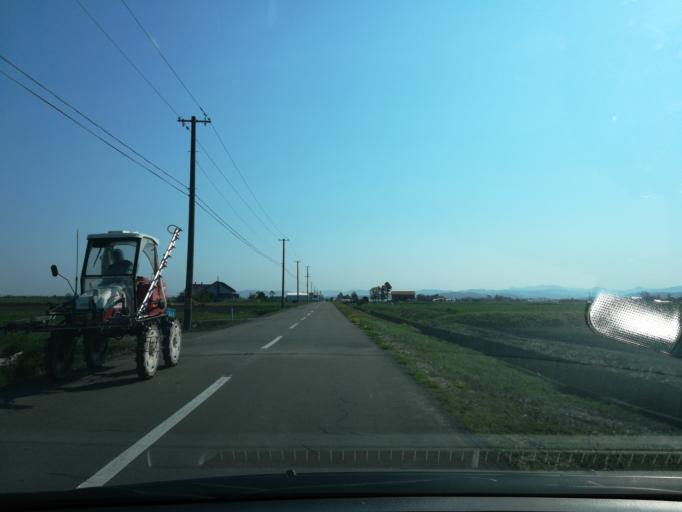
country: JP
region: Hokkaido
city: Iwamizawa
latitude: 43.1393
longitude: 141.6927
